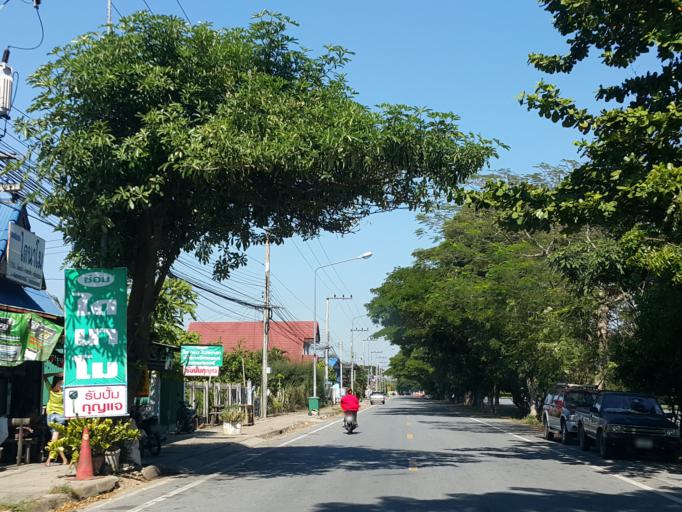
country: TH
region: Lampang
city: Sop Prap
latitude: 17.8945
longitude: 99.3400
